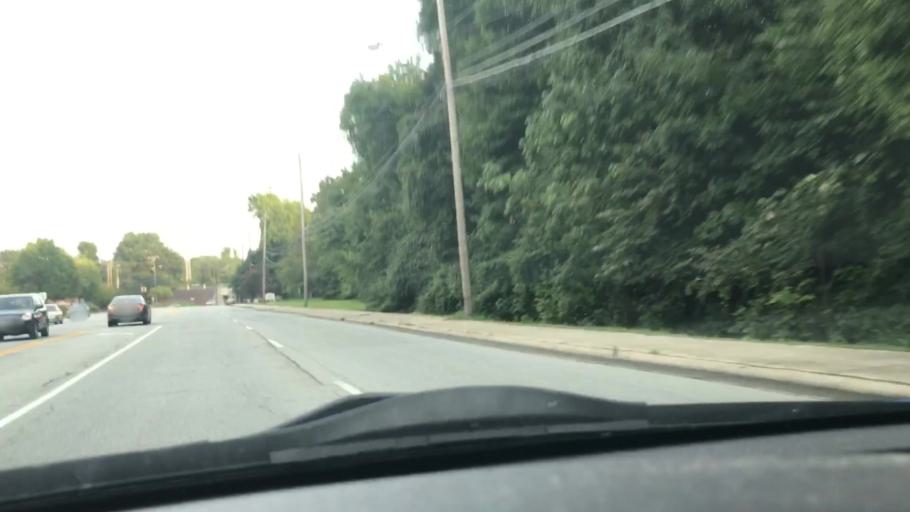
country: US
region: North Carolina
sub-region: Guilford County
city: Greensboro
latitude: 36.0837
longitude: -79.8332
